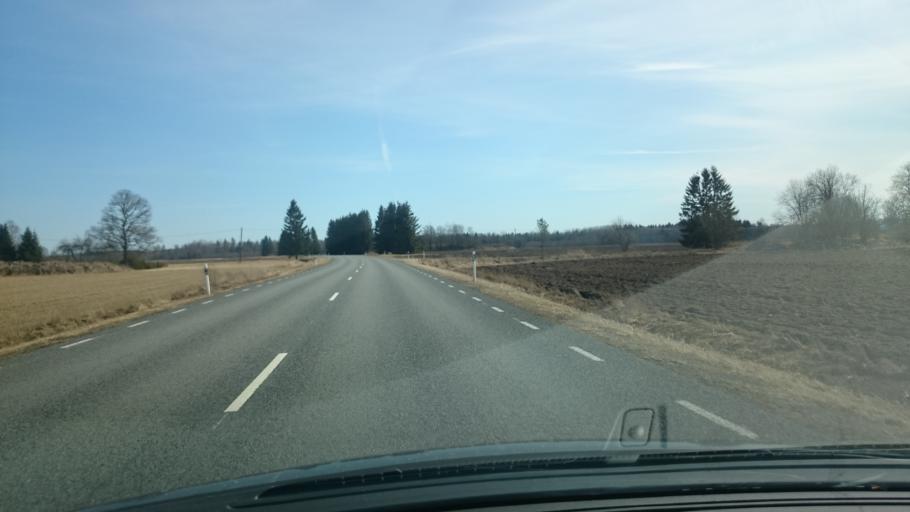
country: EE
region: Paernumaa
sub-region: Tootsi vald
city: Tootsi
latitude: 58.6665
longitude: 24.7821
